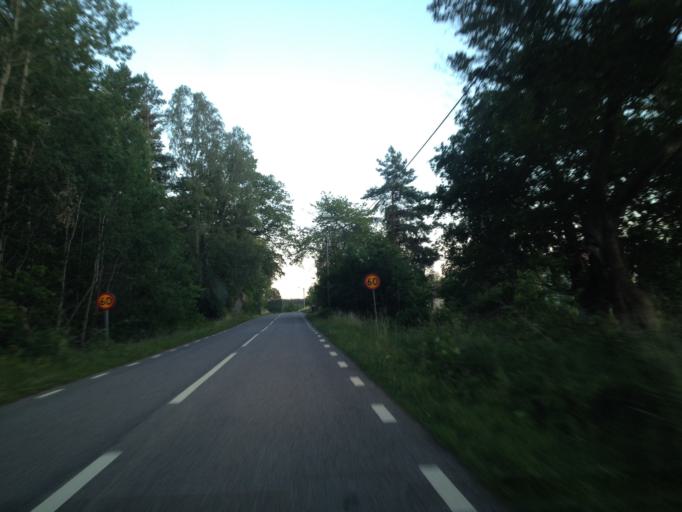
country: SE
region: Kalmar
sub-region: Vasterviks Kommun
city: Overum
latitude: 57.9905
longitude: 16.1872
